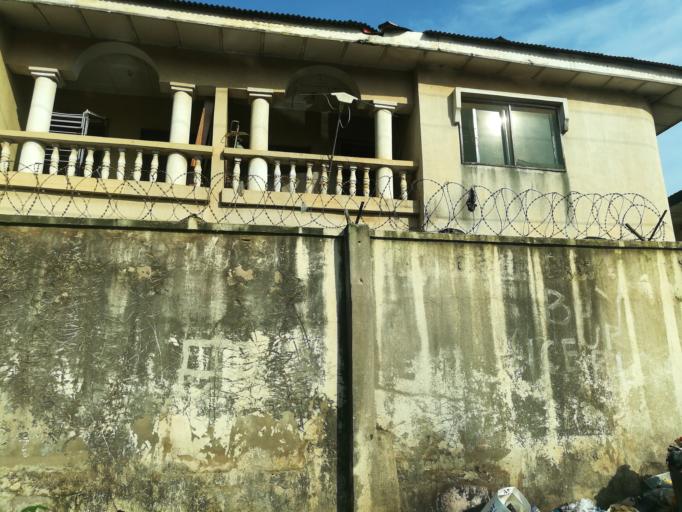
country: NG
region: Lagos
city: Ojota
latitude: 6.6013
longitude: 3.4182
